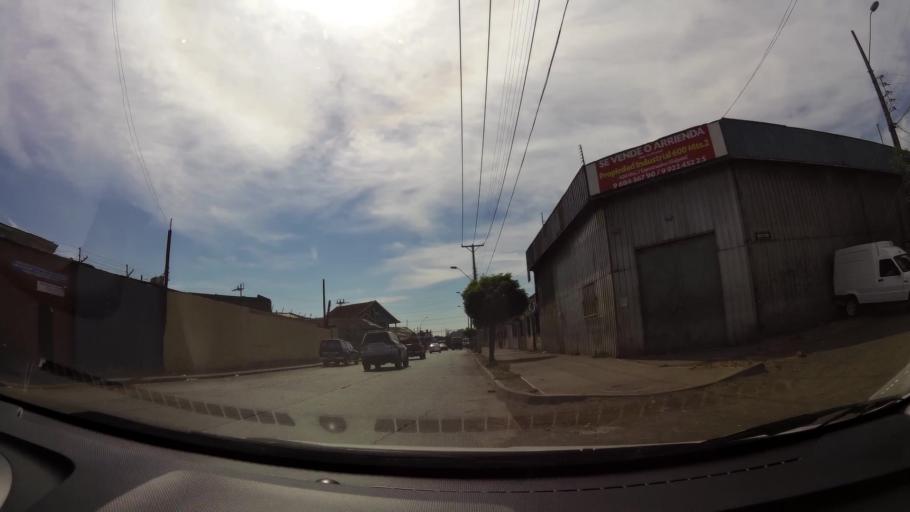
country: CL
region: Biobio
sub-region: Provincia de Concepcion
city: Talcahuano
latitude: -36.7252
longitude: -73.1192
